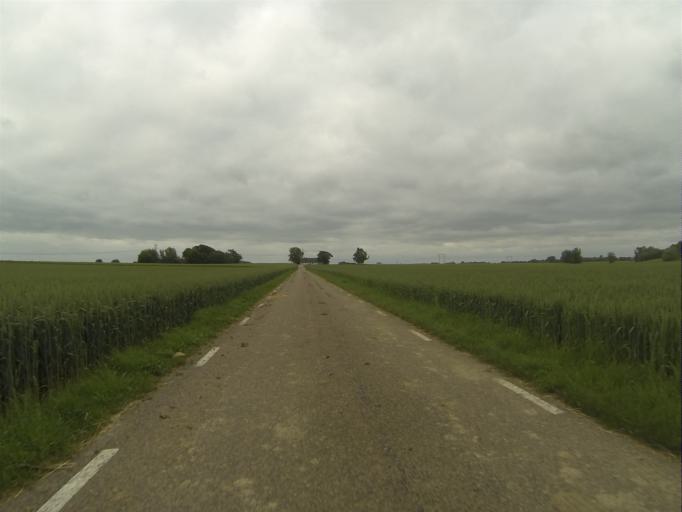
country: SE
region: Skane
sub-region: Staffanstorps Kommun
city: Staffanstorp
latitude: 55.6730
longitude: 13.2454
